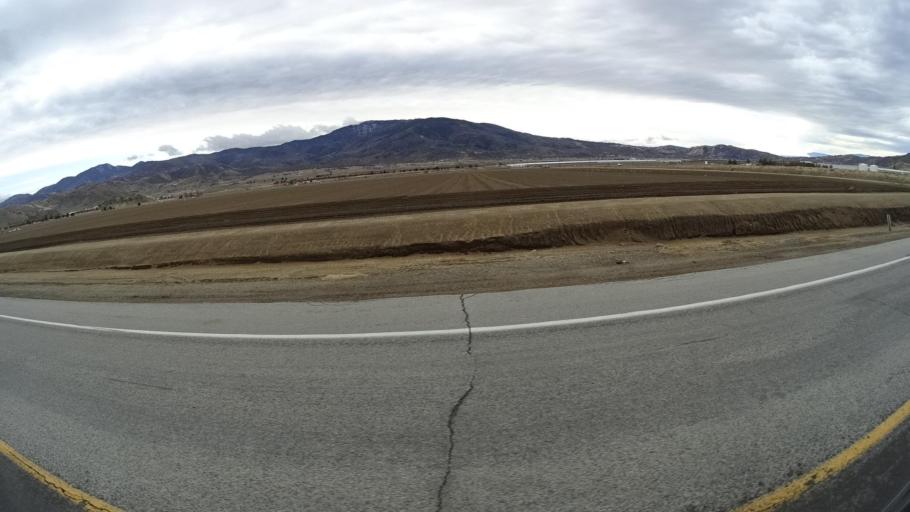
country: US
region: California
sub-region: Kern County
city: Bear Valley Springs
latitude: 35.1317
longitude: -118.5906
